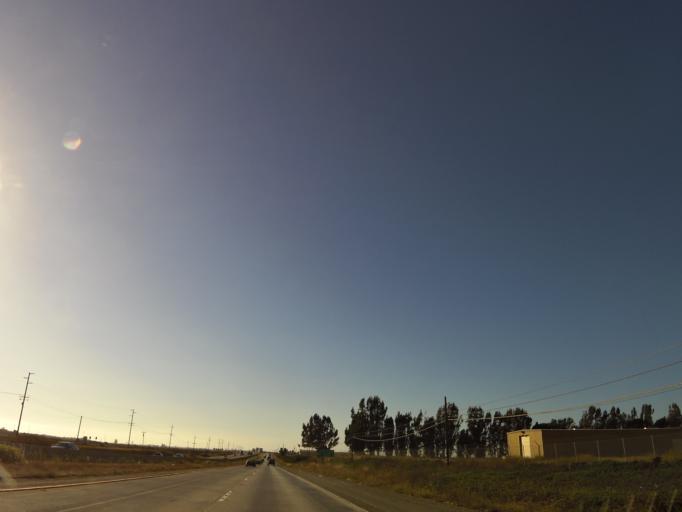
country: US
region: California
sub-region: Monterey County
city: Chualar
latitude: 36.5914
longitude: -121.5411
